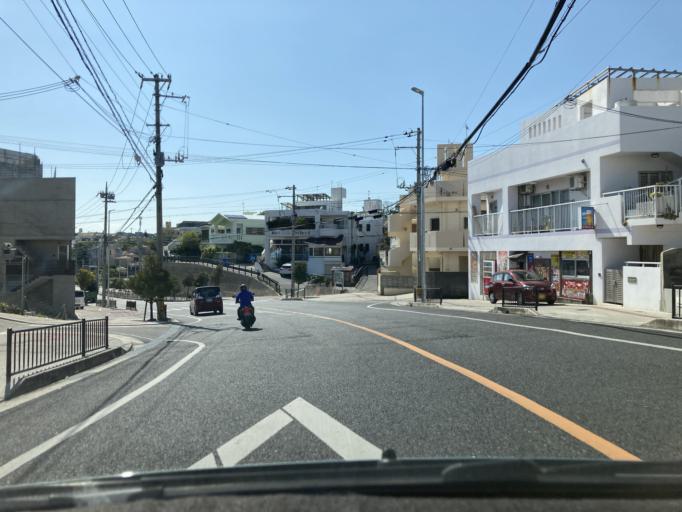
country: JP
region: Okinawa
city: Naha-shi
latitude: 26.2291
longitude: 127.7190
